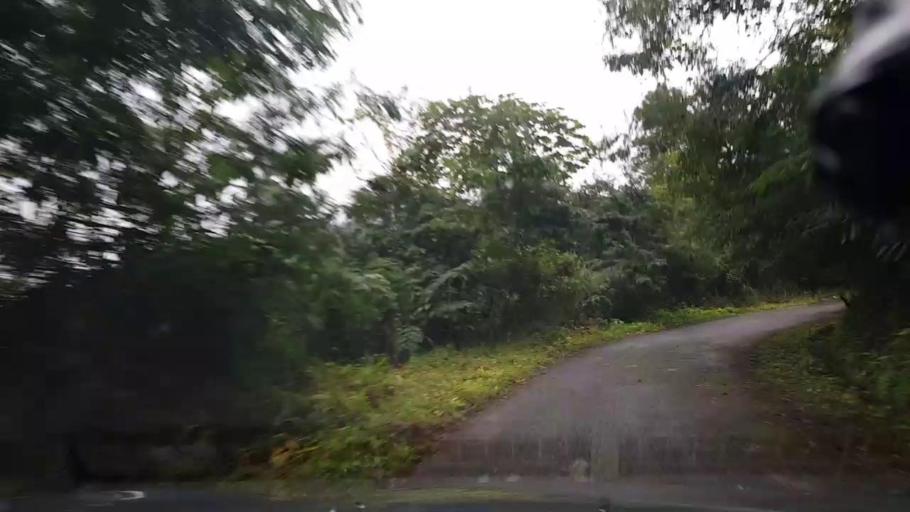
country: JM
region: Saint Andrew
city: Gordon Town
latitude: 18.1053
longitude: -76.7166
